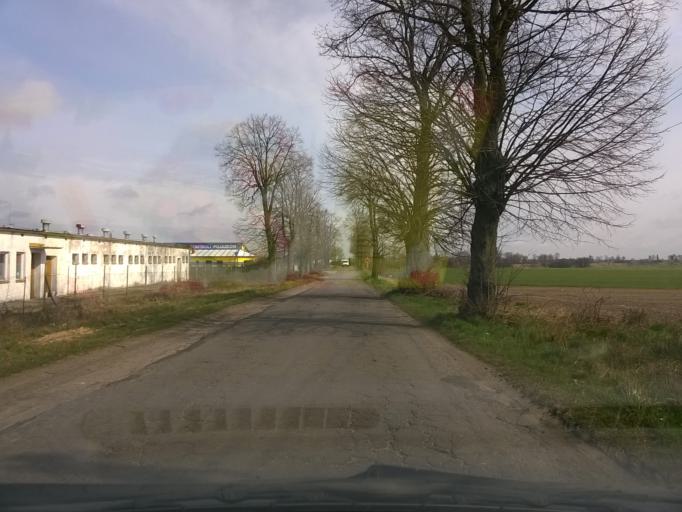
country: PL
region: Greater Poland Voivodeship
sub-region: Powiat wagrowiecki
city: Golancz
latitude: 52.9487
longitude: 17.3168
